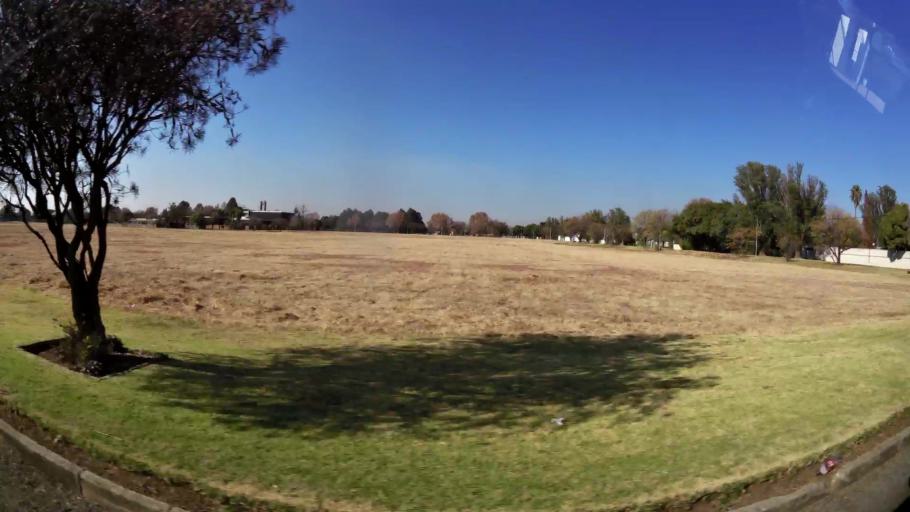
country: ZA
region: Gauteng
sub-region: Ekurhuleni Metropolitan Municipality
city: Benoni
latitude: -26.1556
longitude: 28.3251
